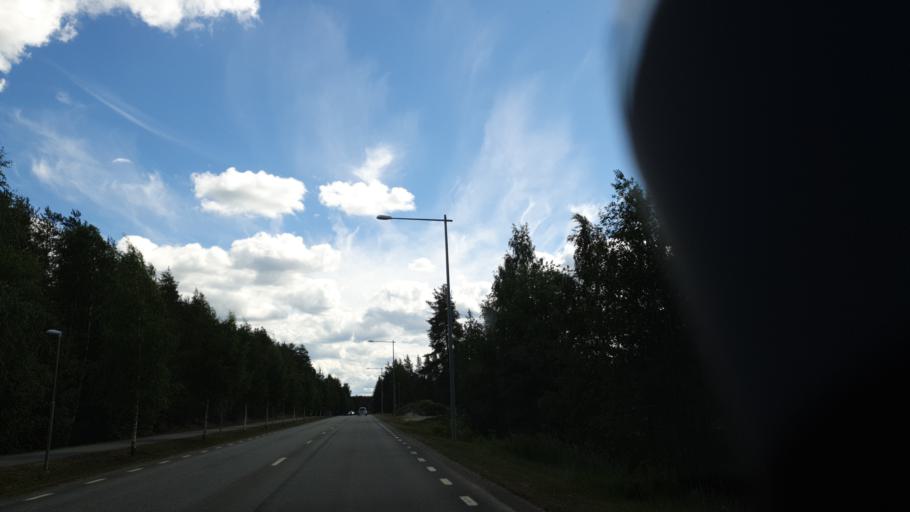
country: SE
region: Vaesterbotten
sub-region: Lycksele Kommun
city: Lycksele
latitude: 64.5841
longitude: 18.6968
